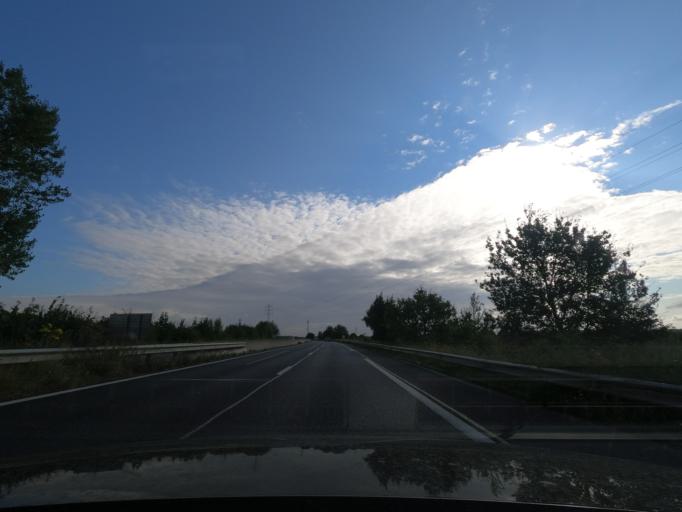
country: FR
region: Haute-Normandie
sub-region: Departement de la Seine-Maritime
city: Isneauville
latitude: 49.4917
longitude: 1.1577
